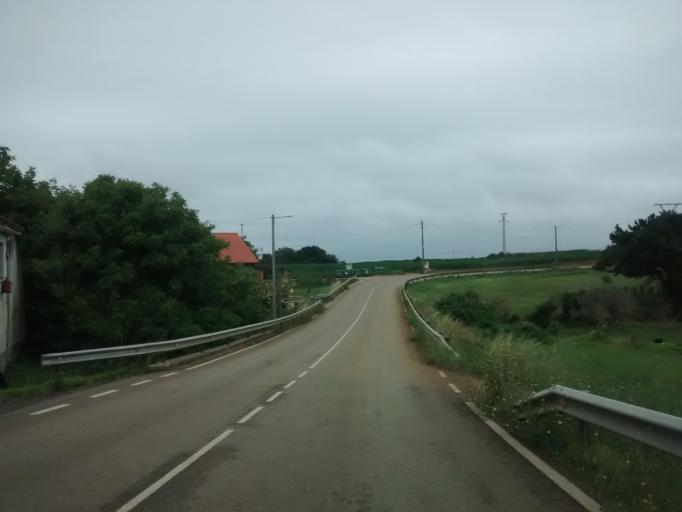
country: ES
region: Cantabria
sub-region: Provincia de Cantabria
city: Santillana
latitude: 43.4114
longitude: -4.1015
